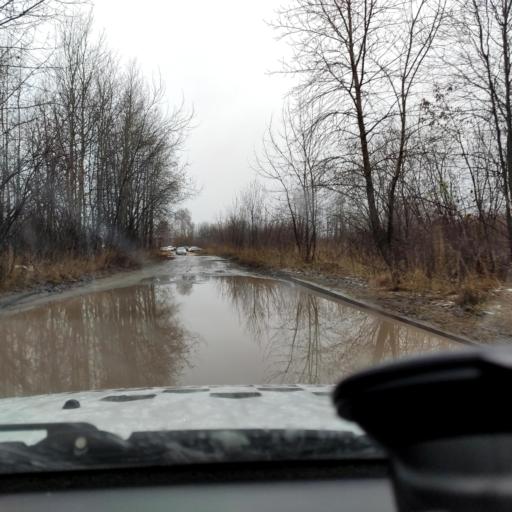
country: RU
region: Perm
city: Perm
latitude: 58.0579
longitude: 56.3261
